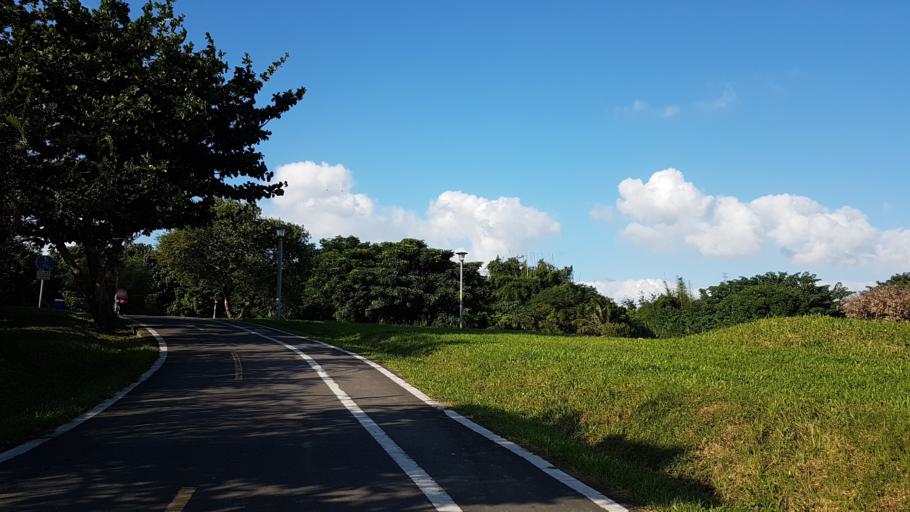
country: TW
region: Taipei
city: Taipei
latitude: 25.0042
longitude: 121.5307
